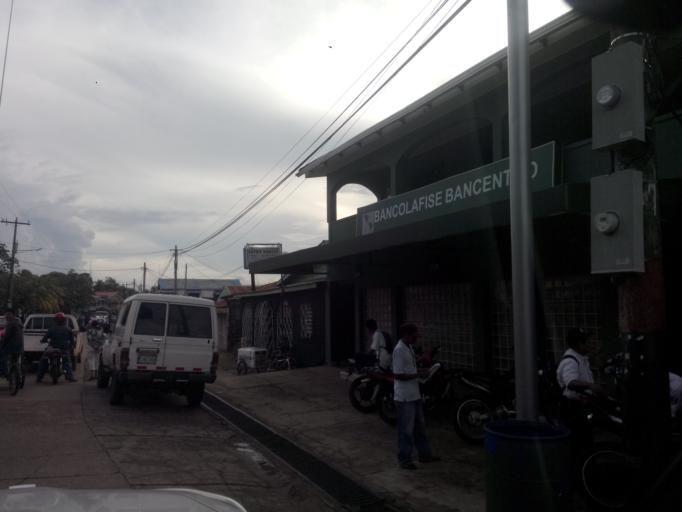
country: NI
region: Atlantico Norte (RAAN)
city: Puerto Cabezas
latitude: 14.0308
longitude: -83.3798
